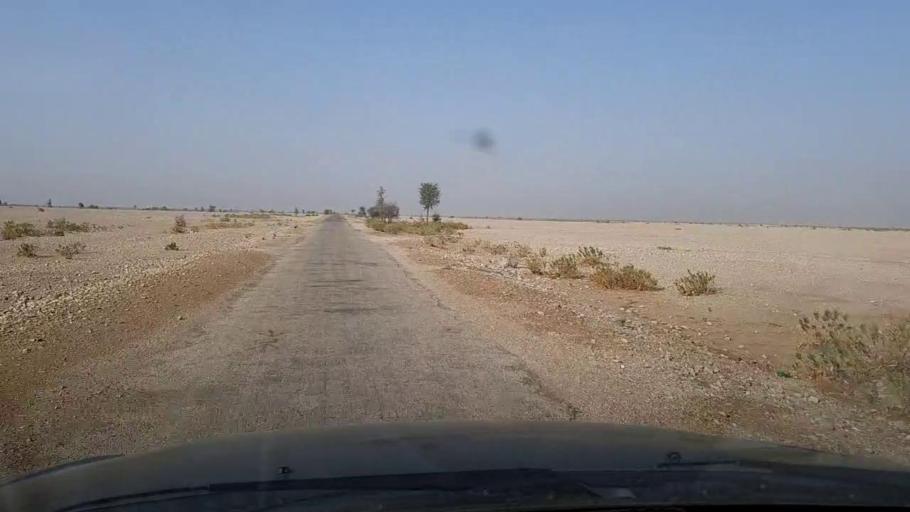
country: PK
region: Sindh
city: Sann
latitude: 25.9983
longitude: 68.0755
